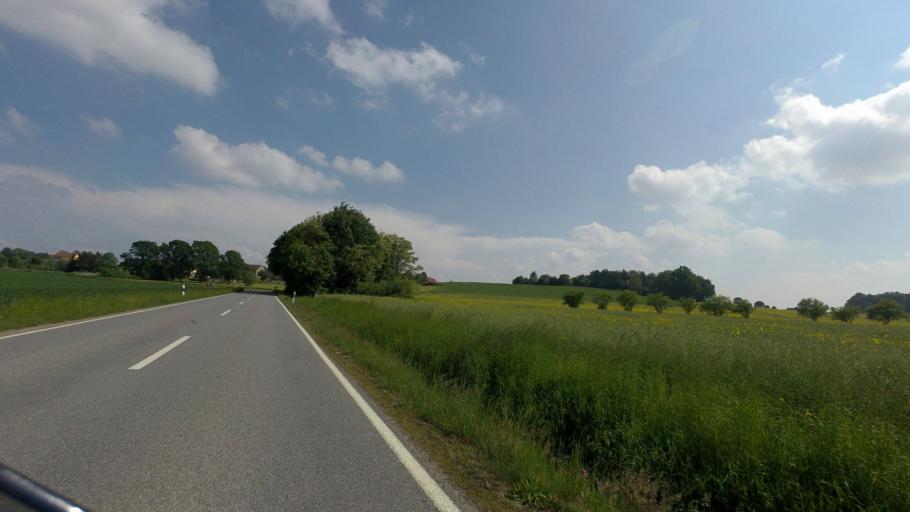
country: DE
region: Saxony
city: Guttau
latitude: 51.2158
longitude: 14.6018
